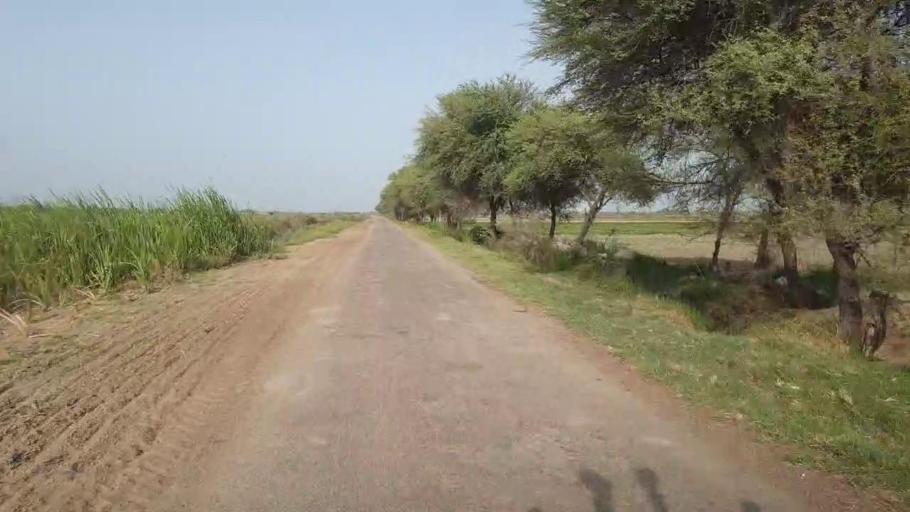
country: PK
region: Sindh
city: Daur
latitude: 26.3402
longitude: 68.2278
